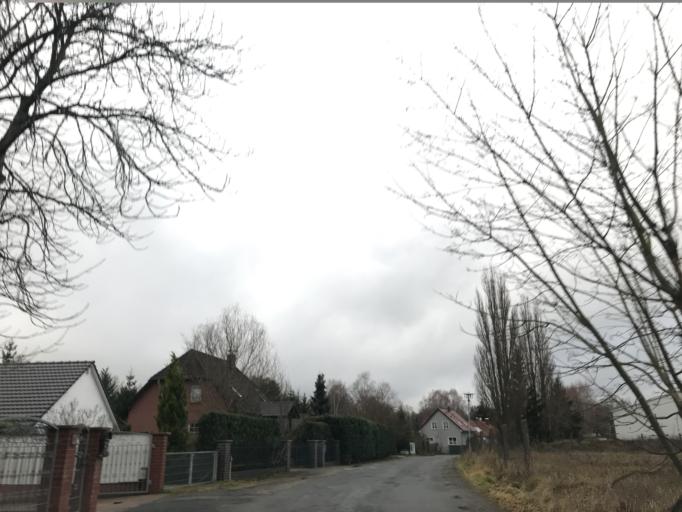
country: DE
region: Brandenburg
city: Rheinsberg
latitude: 53.0937
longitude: 12.8973
